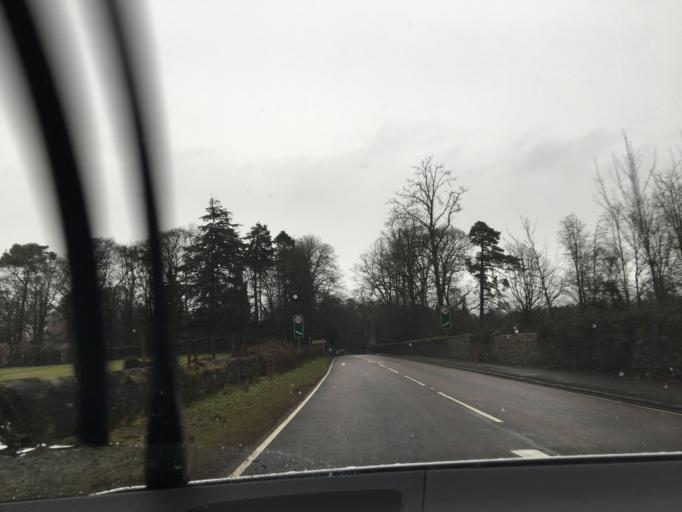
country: GB
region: Scotland
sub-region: Stirling
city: Doune
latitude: 56.1843
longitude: -4.0635
